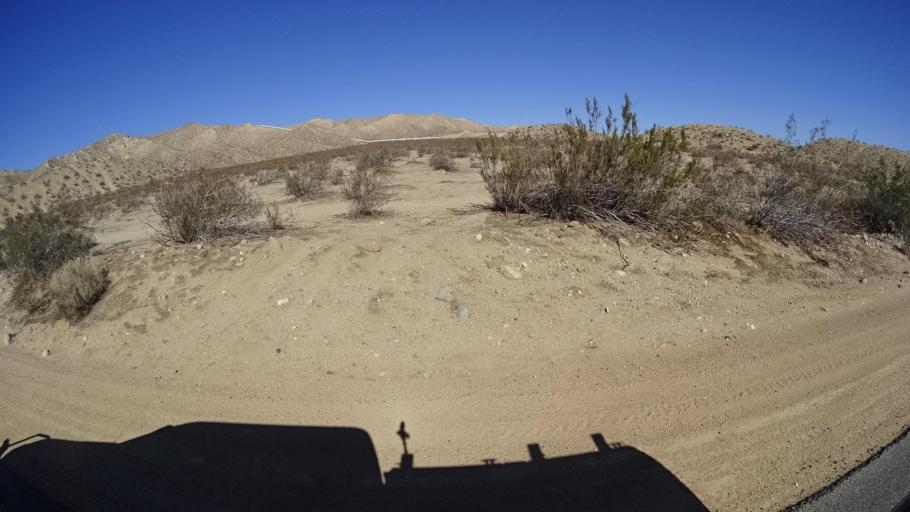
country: US
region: California
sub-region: Kern County
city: California City
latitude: 35.3104
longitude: -118.0195
